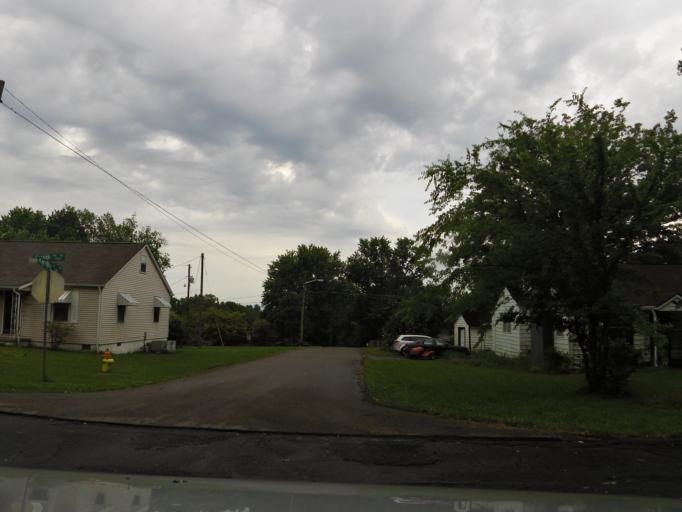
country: US
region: Tennessee
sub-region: Knox County
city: Knoxville
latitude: 36.0000
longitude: -83.9028
